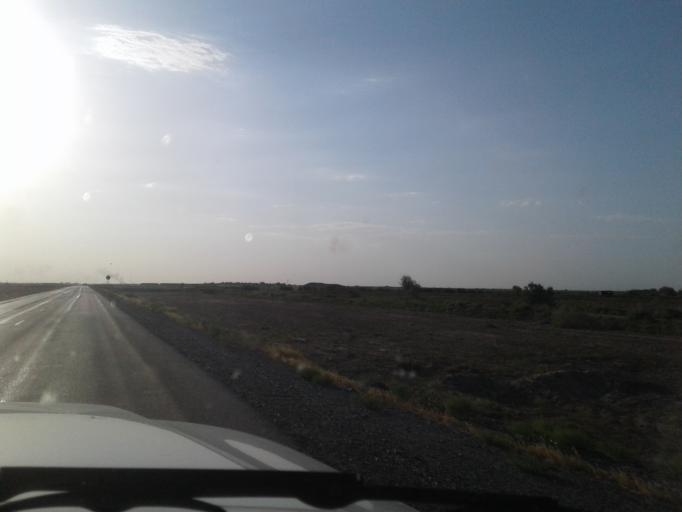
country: TM
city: Murgab
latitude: 37.4544
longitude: 62.0654
